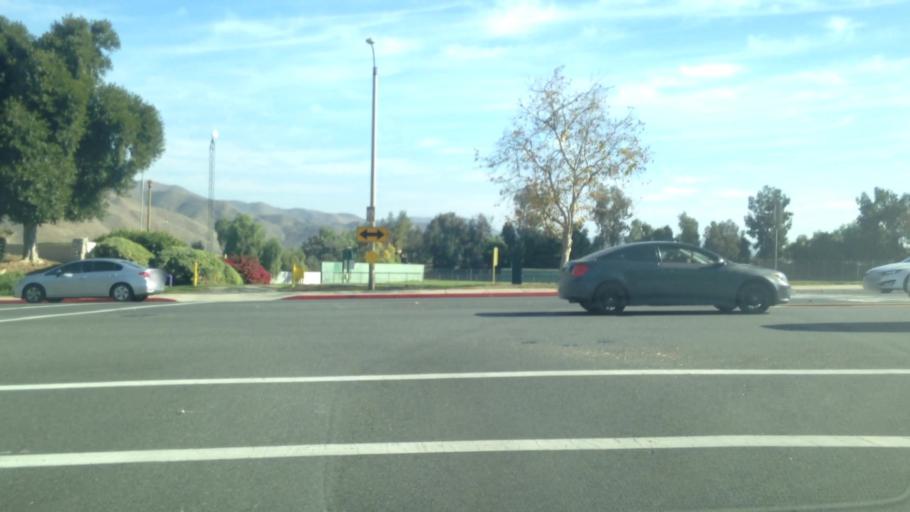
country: US
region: California
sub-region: Riverside County
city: Lake Elsinore
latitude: 33.7343
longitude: -117.4295
